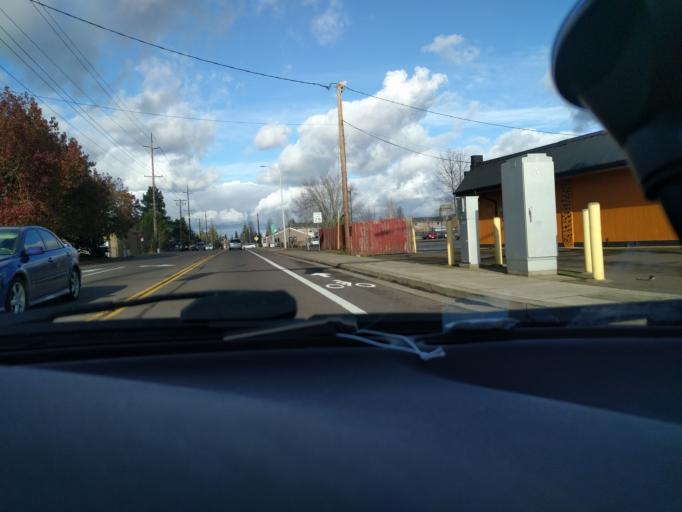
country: US
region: Oregon
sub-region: Marion County
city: Hayesville
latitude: 44.9682
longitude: -122.9917
